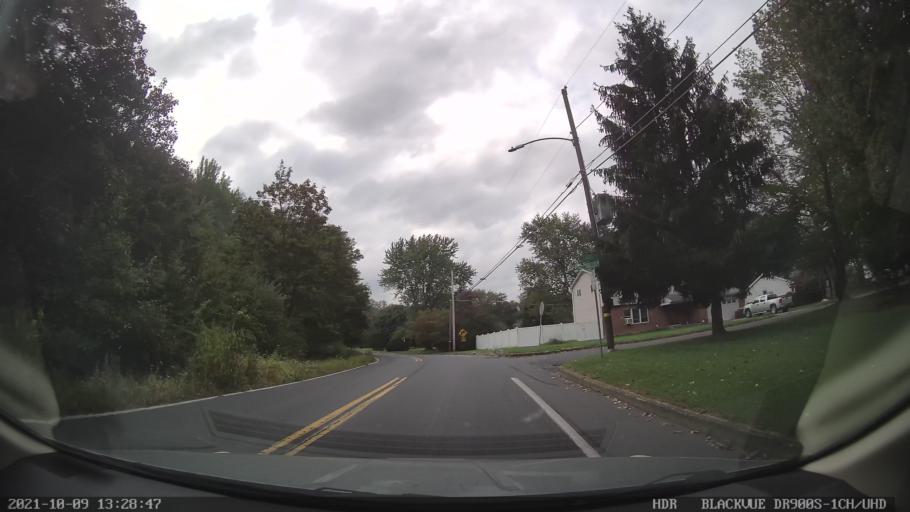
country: US
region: Pennsylvania
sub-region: Lehigh County
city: Ancient Oaks
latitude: 40.5391
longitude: -75.5924
